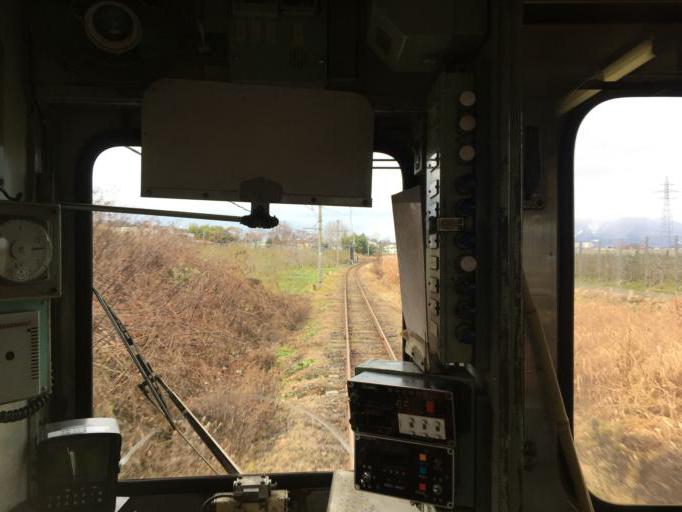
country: JP
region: Aomori
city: Hirosaki
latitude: 40.5594
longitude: 140.5027
